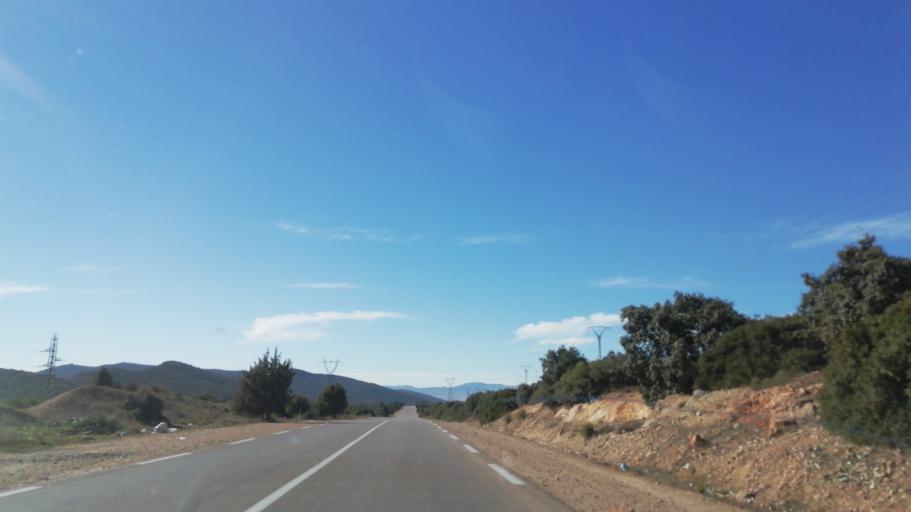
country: DZ
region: Tlemcen
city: Sebdou
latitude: 34.7196
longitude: -1.2008
